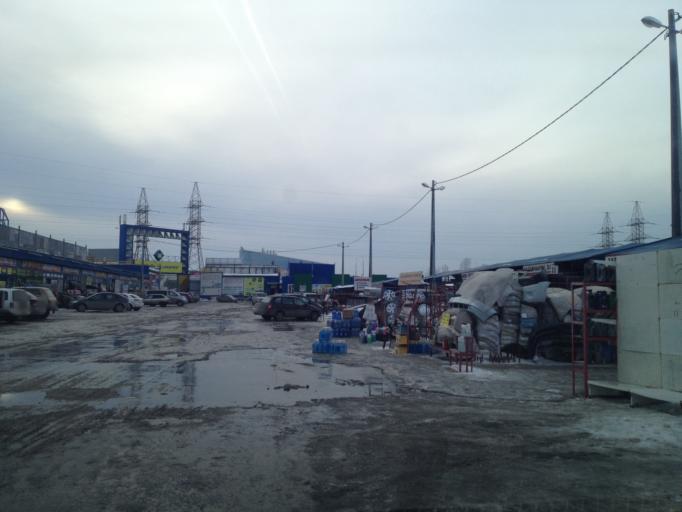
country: RU
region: Sverdlovsk
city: Shirokaya Rechka
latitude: 56.8278
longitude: 60.5174
